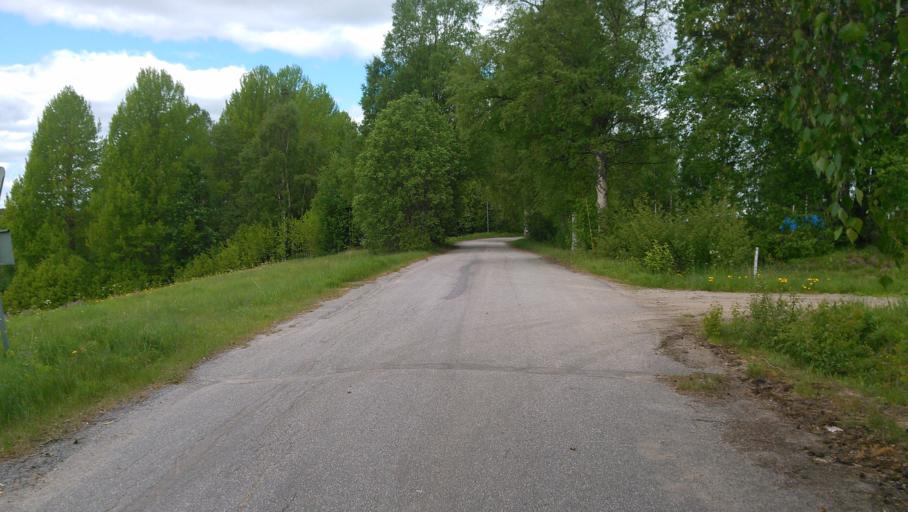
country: SE
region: Vaesterbotten
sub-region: Umea Kommun
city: Roback
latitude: 63.8583
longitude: 20.0906
